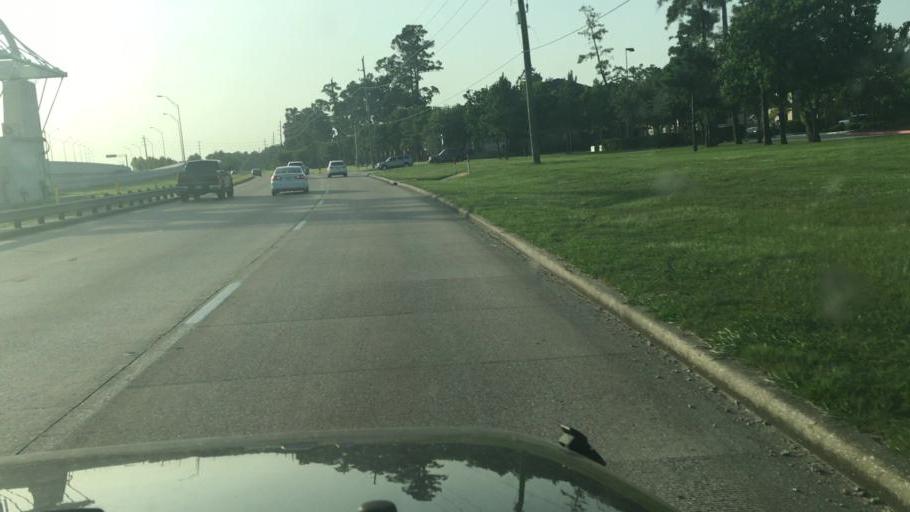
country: US
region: Texas
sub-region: Harris County
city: Atascocita
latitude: 29.9278
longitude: -95.2010
